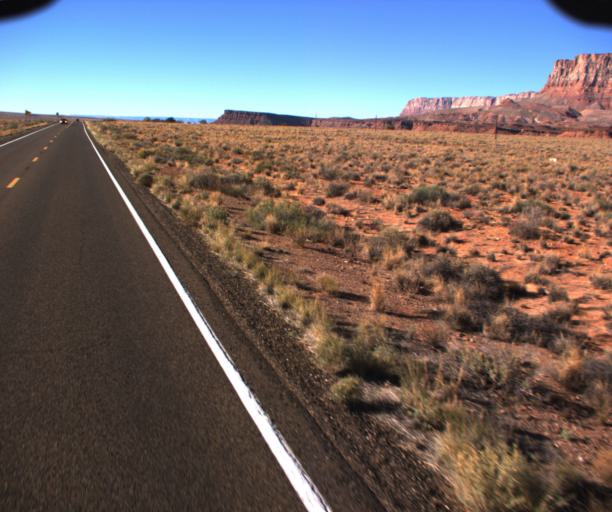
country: US
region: Arizona
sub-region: Coconino County
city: Page
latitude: 36.7967
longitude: -111.6797
